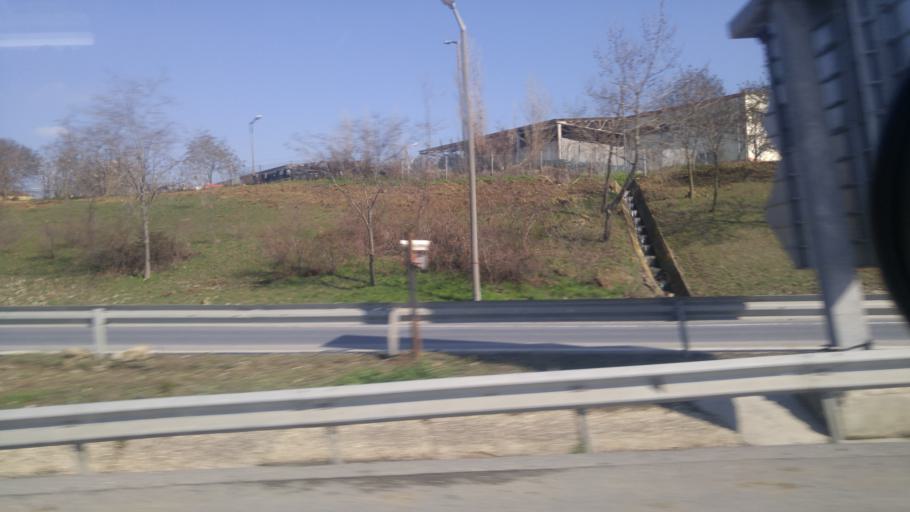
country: TR
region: Istanbul
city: Ortakoy
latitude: 41.0814
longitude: 28.3712
